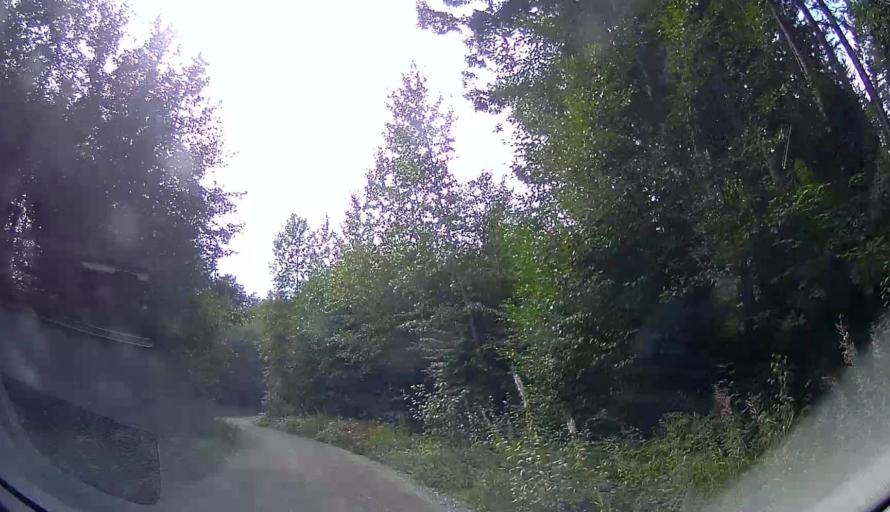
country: US
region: Washington
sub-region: Whatcom County
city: Sudden Valley
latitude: 48.6192
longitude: -122.3773
